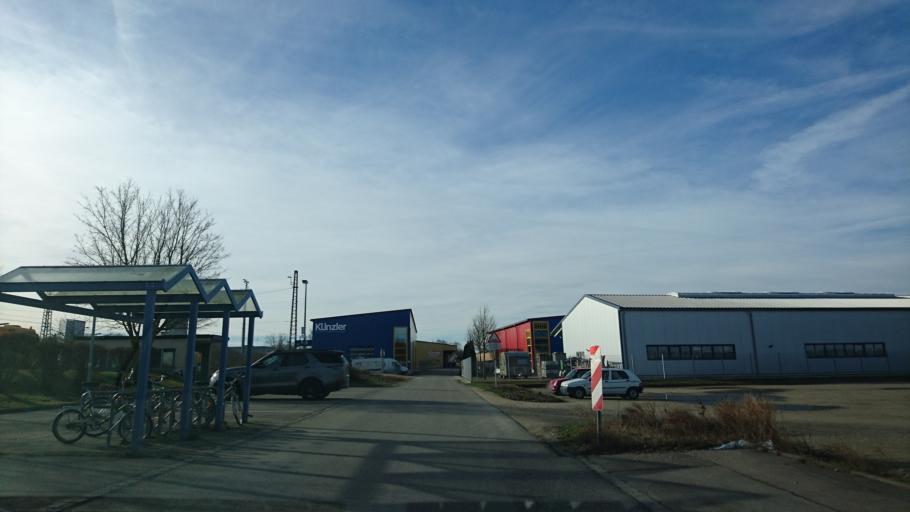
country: DE
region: Bavaria
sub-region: Swabia
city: Meitingen
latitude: 48.5461
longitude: 10.8475
